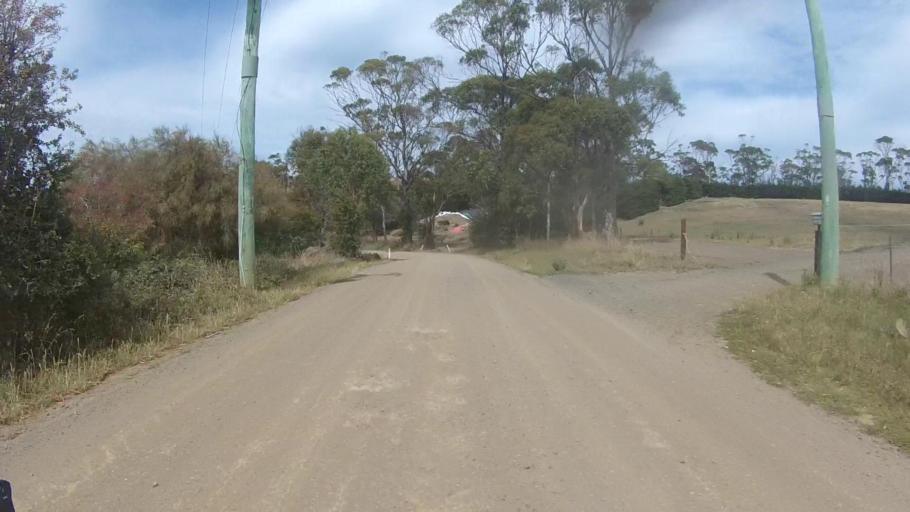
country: AU
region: Tasmania
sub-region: Sorell
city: Sorell
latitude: -42.8181
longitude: 147.8242
